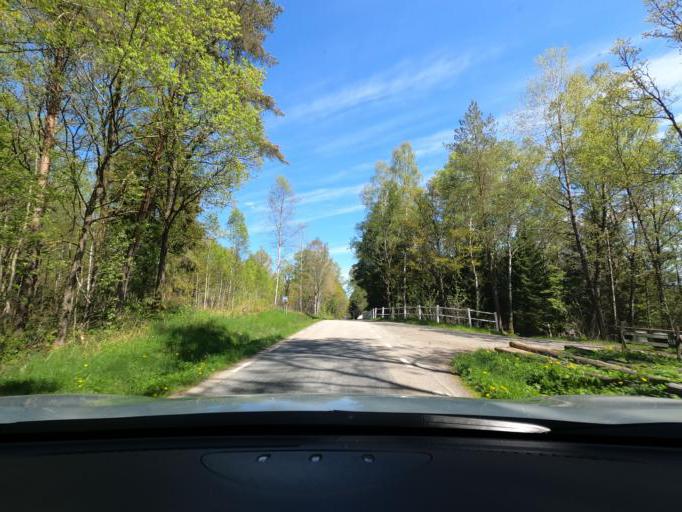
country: SE
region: Vaestra Goetaland
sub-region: Marks Kommun
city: Horred
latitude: 57.4311
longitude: 12.4100
